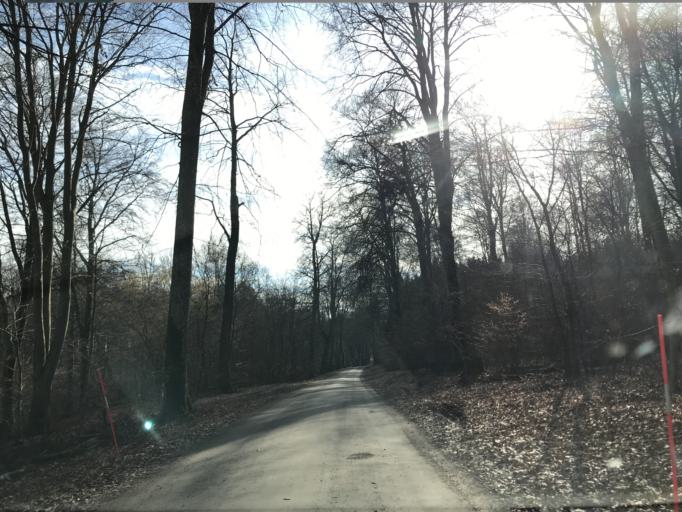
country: SE
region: Skane
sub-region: Tomelilla Kommun
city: Tomelilla
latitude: 55.5242
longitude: 13.8904
